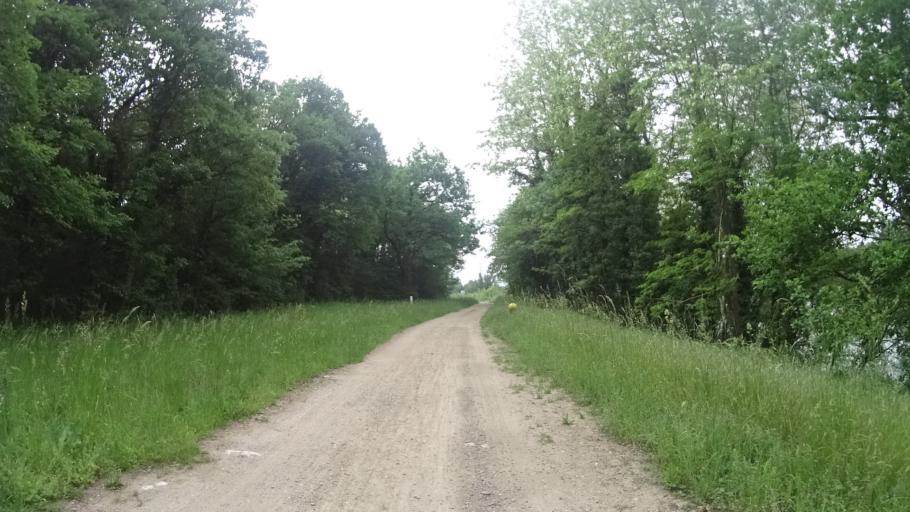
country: FR
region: Alsace
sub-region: Departement du Haut-Rhin
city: Kembs
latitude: 47.6836
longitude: 7.5208
